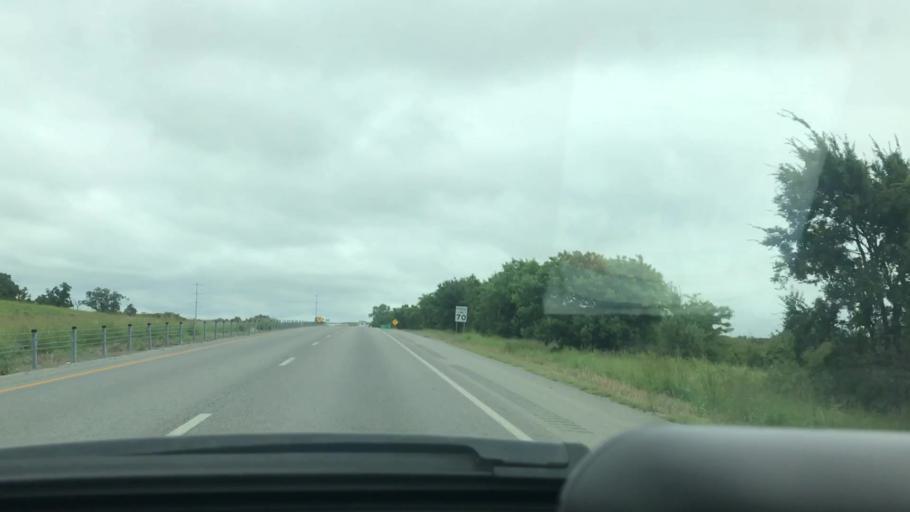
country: US
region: Oklahoma
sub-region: Coal County
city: Coalgate
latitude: 34.6690
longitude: -95.9369
